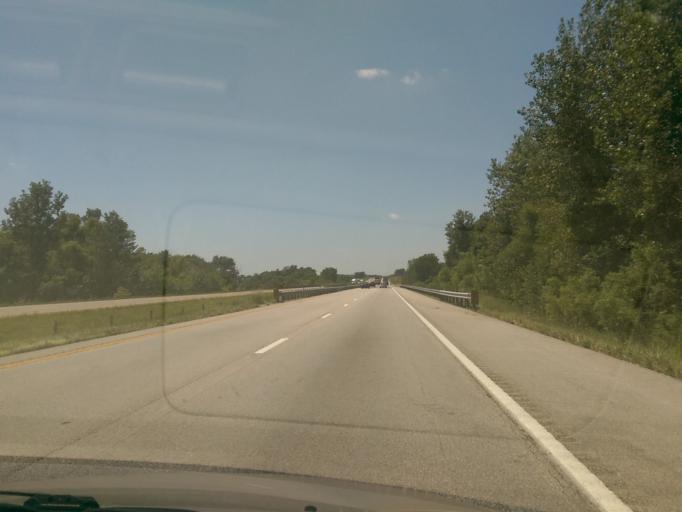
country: US
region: Missouri
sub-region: Cooper County
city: Boonville
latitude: 38.9350
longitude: -92.8977
